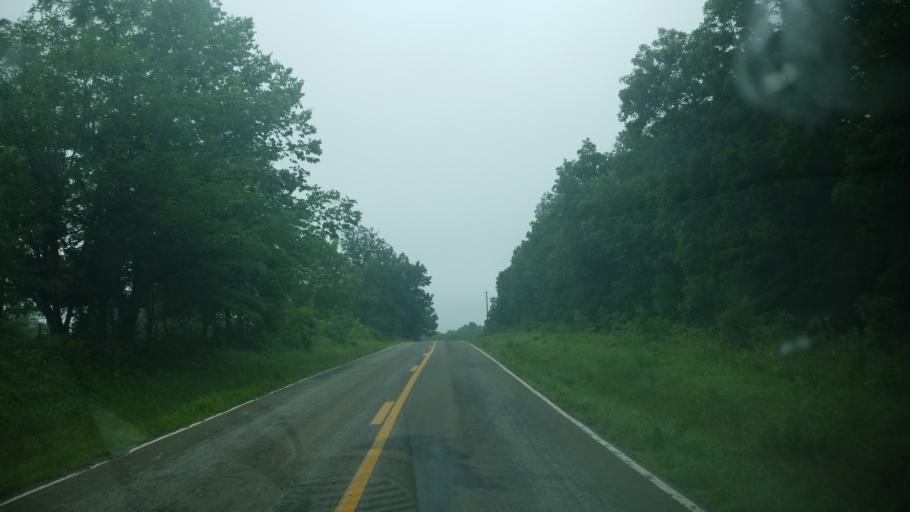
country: US
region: Missouri
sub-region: Audrain County
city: Vandalia
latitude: 39.2928
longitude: -91.3507
